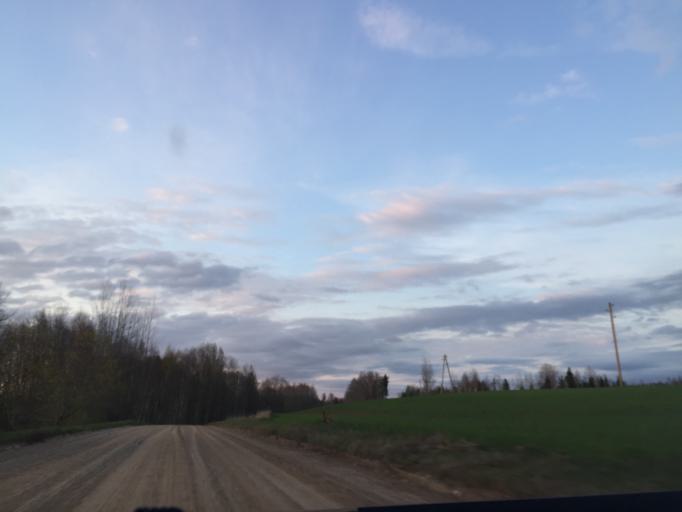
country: LV
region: Aluksnes Rajons
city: Aluksne
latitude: 57.3263
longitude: 26.9433
